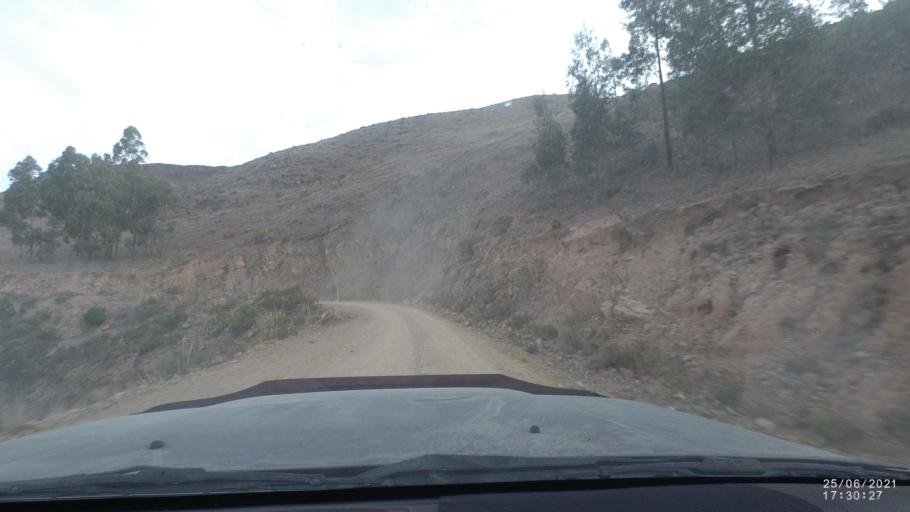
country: BO
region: Cochabamba
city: Mizque
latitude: -17.9338
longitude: -65.6657
